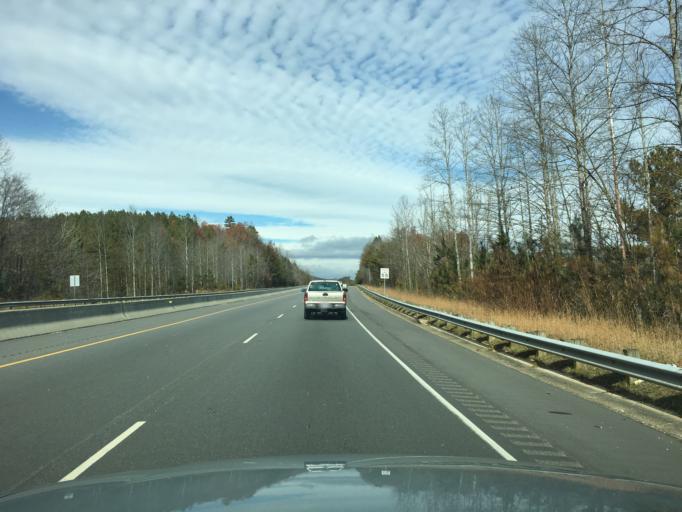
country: US
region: North Carolina
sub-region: McDowell County
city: Marion
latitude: 35.6878
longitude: -82.0305
